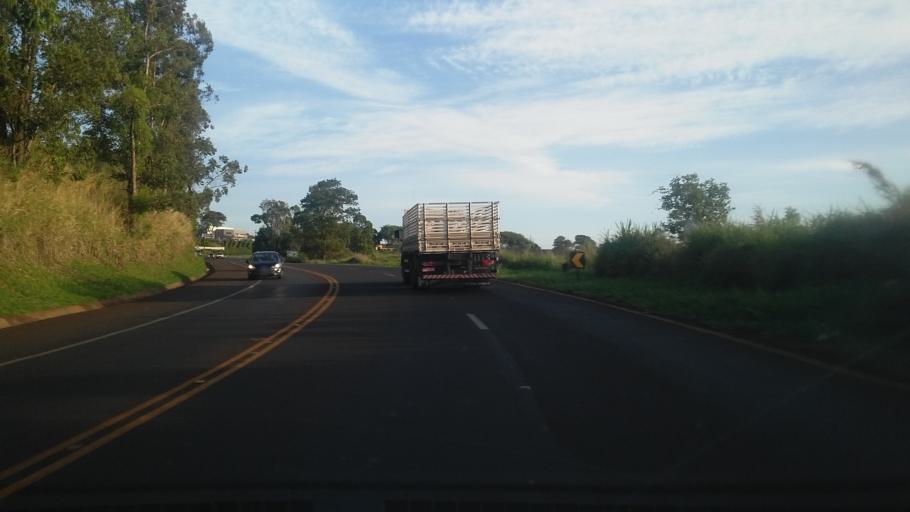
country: BR
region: Parana
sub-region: Bandeirantes
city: Bandeirantes
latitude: -23.1785
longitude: -50.6230
